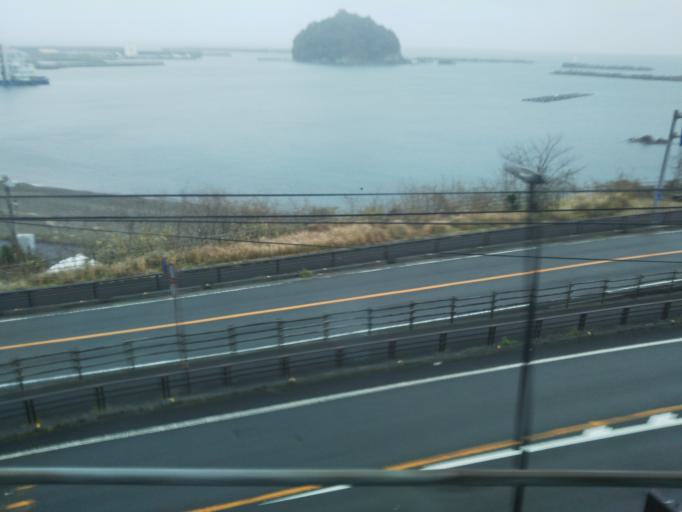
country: JP
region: Kochi
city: Nakamura
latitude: 33.0723
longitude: 133.1041
